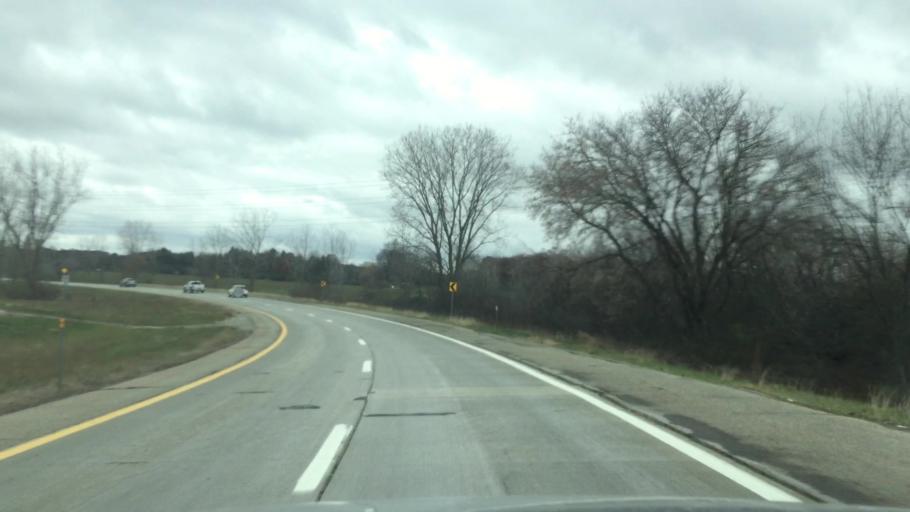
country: US
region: Michigan
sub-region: Washtenaw County
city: Ypsilanti
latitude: 42.3279
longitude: -83.6354
